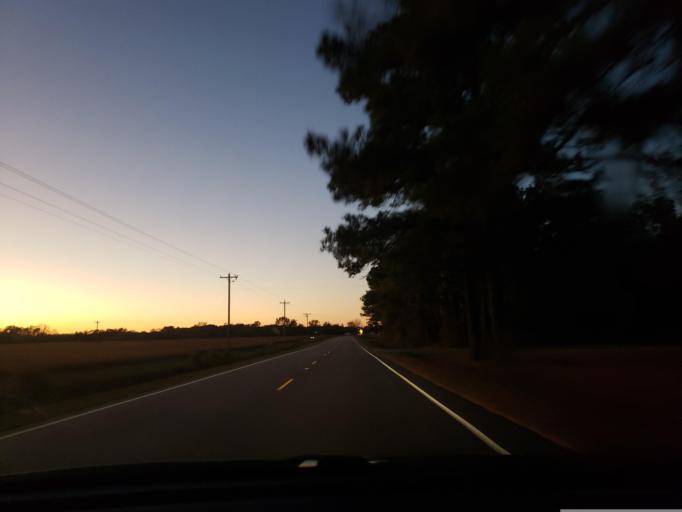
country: US
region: North Carolina
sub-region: Duplin County
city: Kenansville
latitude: 34.9077
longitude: -77.9249
